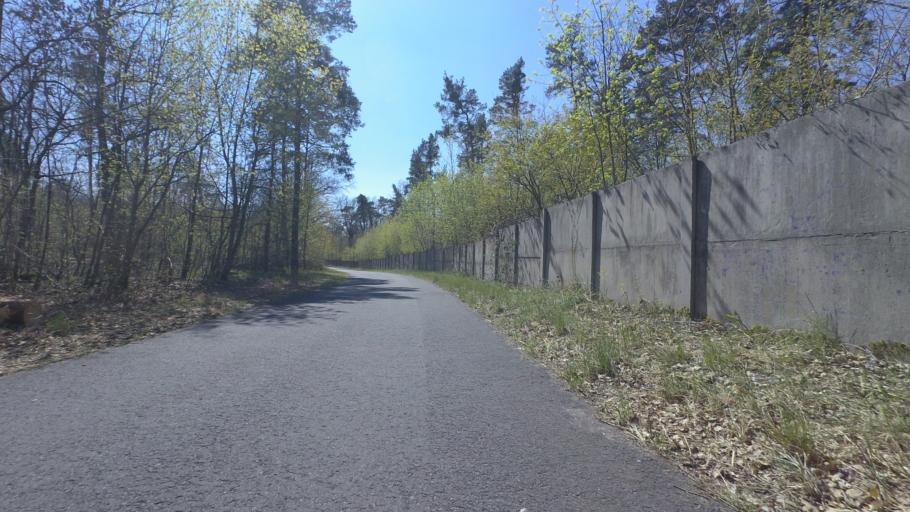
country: DE
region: Brandenburg
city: Zossen
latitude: 52.1959
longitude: 13.4777
